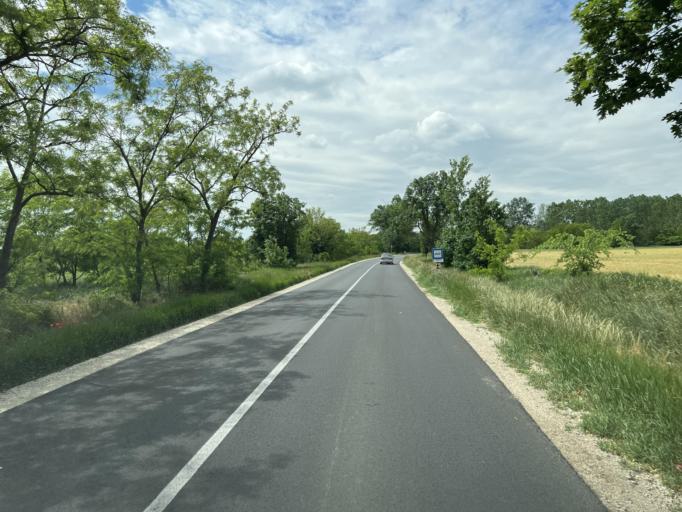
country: HU
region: Pest
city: Suelysap
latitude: 47.4625
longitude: 19.5538
